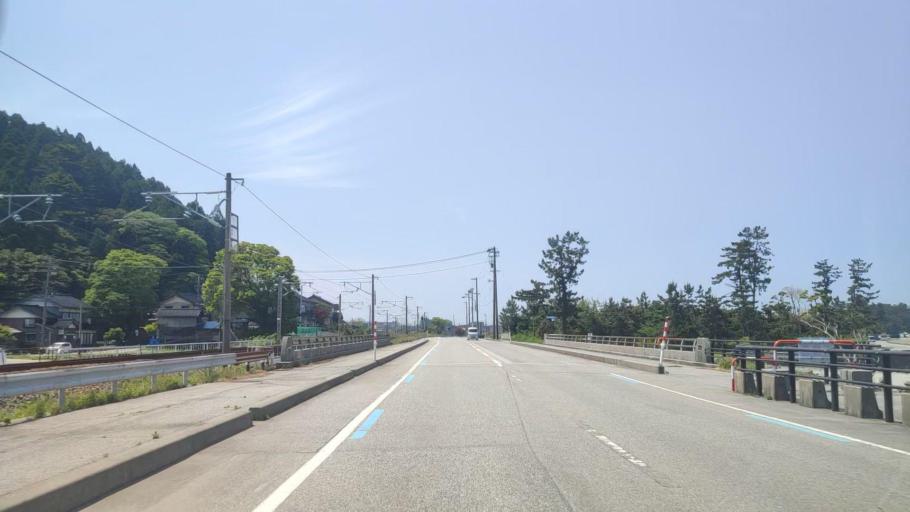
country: JP
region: Toyama
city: Nyuzen
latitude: 36.9641
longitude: 137.5751
